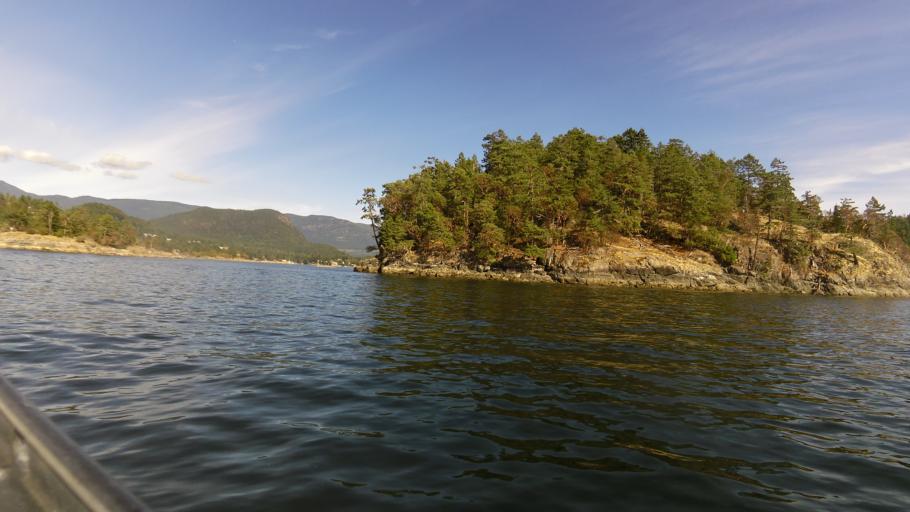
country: CA
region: British Columbia
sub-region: Sunshine Coast Regional District
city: Sechelt
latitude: 49.6271
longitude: -124.0602
